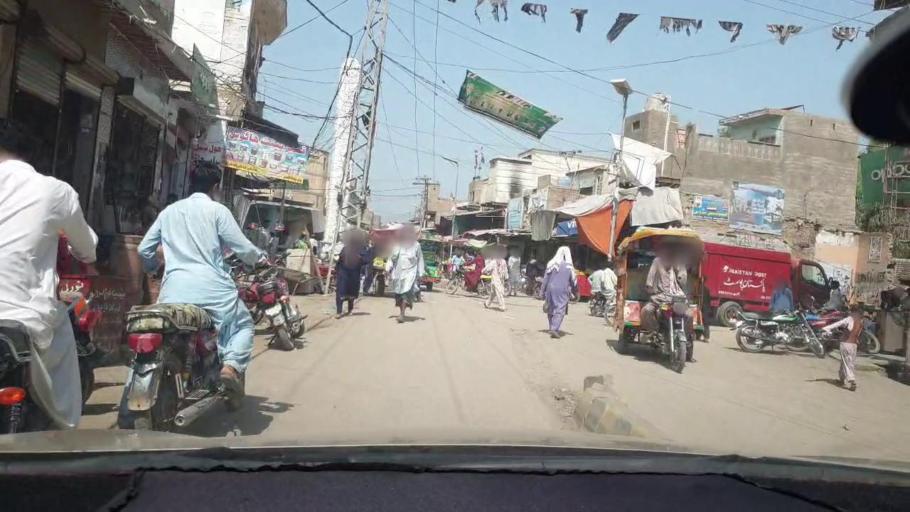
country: PK
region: Sindh
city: Kambar
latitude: 27.5899
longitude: 68.0026
